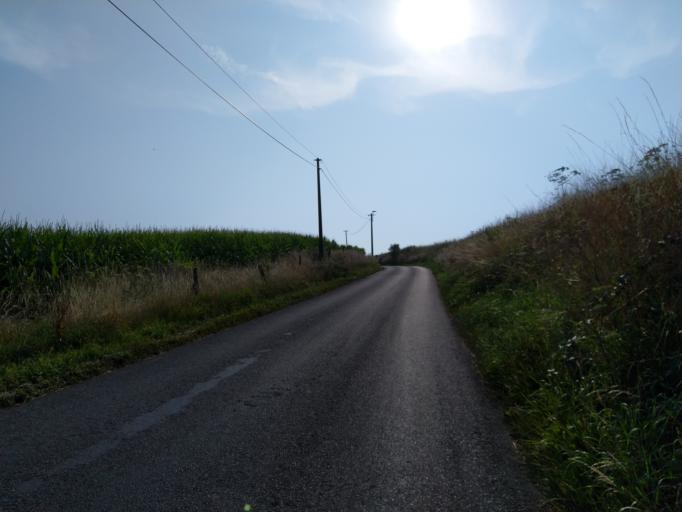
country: BE
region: Wallonia
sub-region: Province du Hainaut
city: Ecaussinnes-d'Enghien
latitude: 50.6094
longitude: 4.2052
